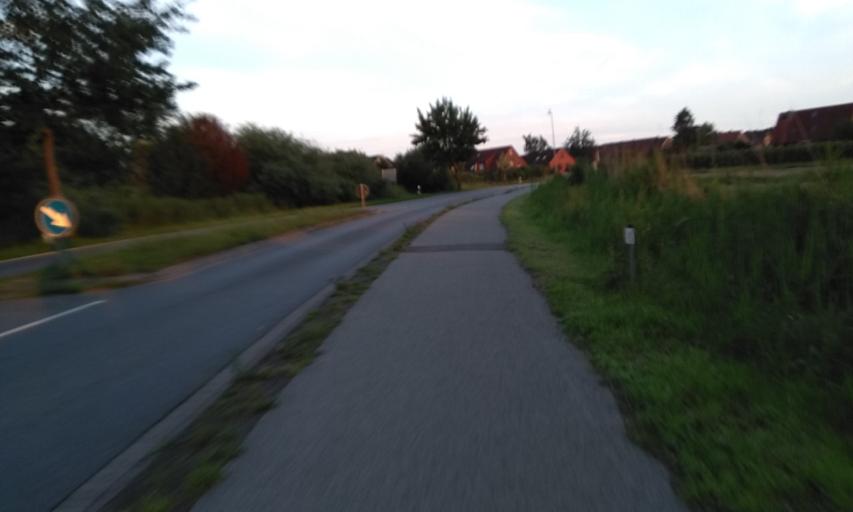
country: DE
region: Lower Saxony
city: Jork
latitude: 53.5077
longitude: 9.7293
